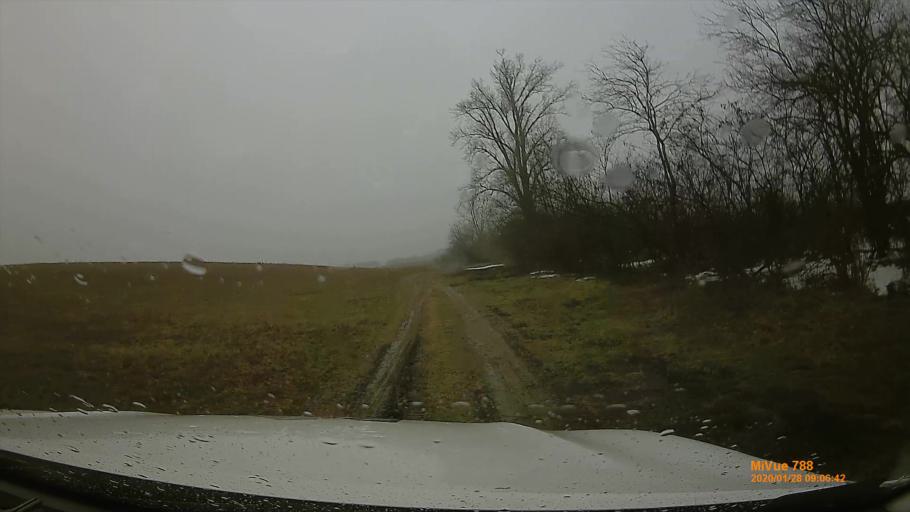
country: HU
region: Pest
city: Pilis
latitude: 47.3189
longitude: 19.5382
